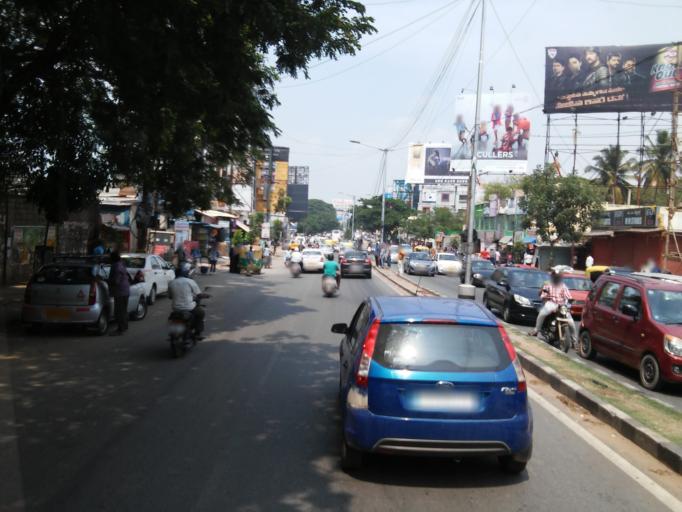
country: IN
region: Karnataka
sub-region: Bangalore Urban
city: Bangalore
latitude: 12.9594
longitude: 77.6551
